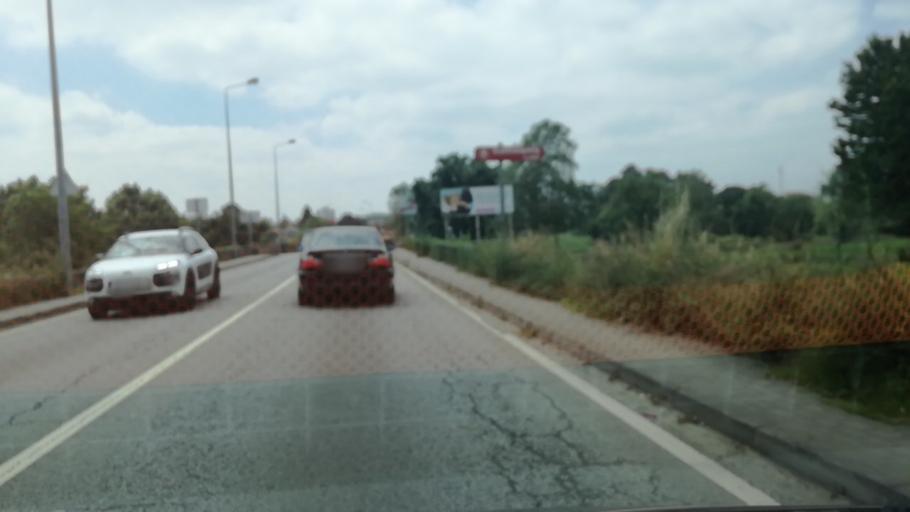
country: PT
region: Braga
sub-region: Vila Nova de Famalicao
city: Ferreiros
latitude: 41.3463
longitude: -8.5563
